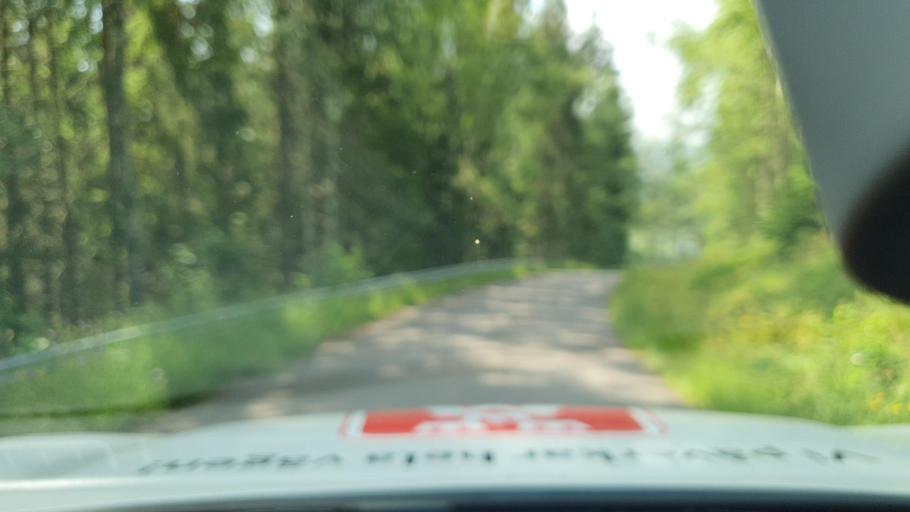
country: SE
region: Vaermland
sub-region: Sunne Kommun
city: Sunne
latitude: 59.9762
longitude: 13.0942
